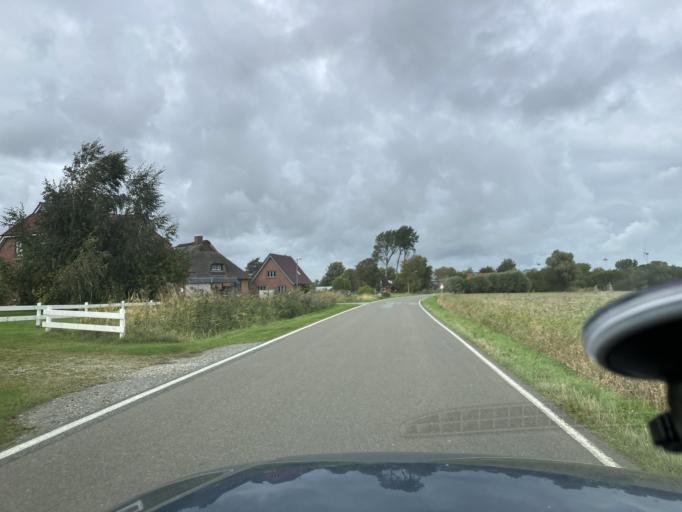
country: DE
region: Schleswig-Holstein
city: Wesselburener Deichhausen
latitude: 54.1779
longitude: 8.9392
